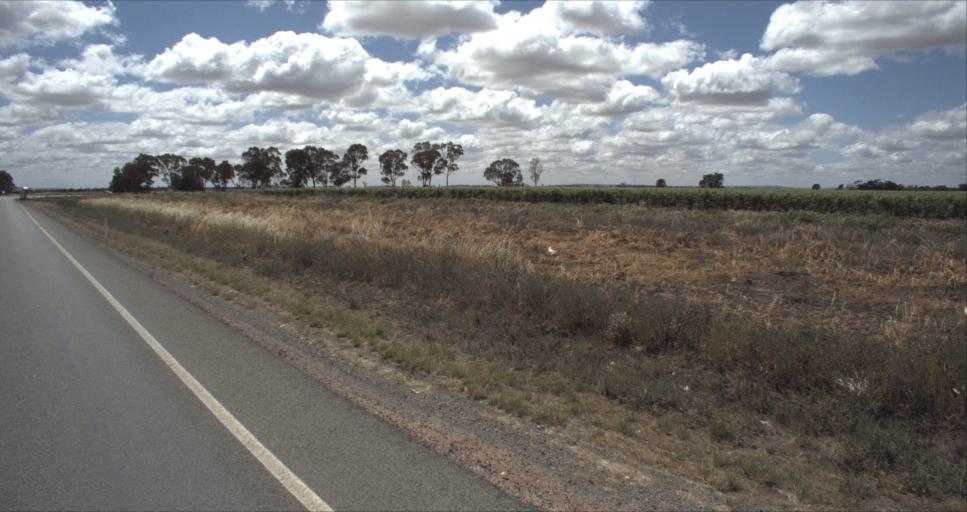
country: AU
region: New South Wales
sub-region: Murrumbidgee Shire
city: Darlington Point
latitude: -34.5053
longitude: 146.1873
